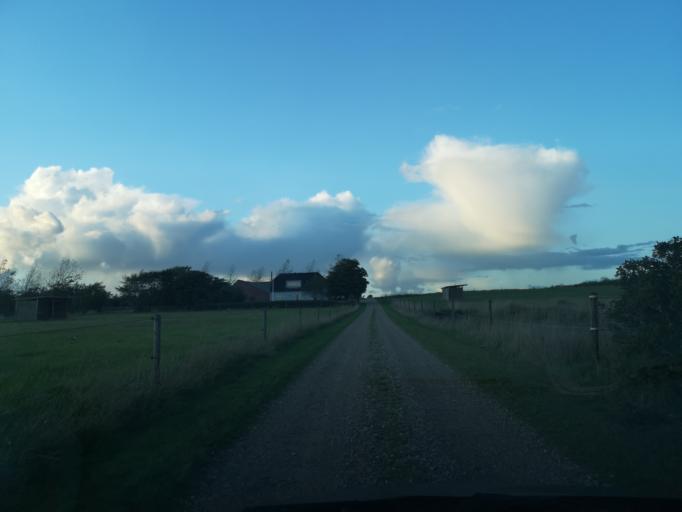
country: DK
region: Central Jutland
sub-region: Ringkobing-Skjern Kommune
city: Videbaek
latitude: 56.0477
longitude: 8.5885
